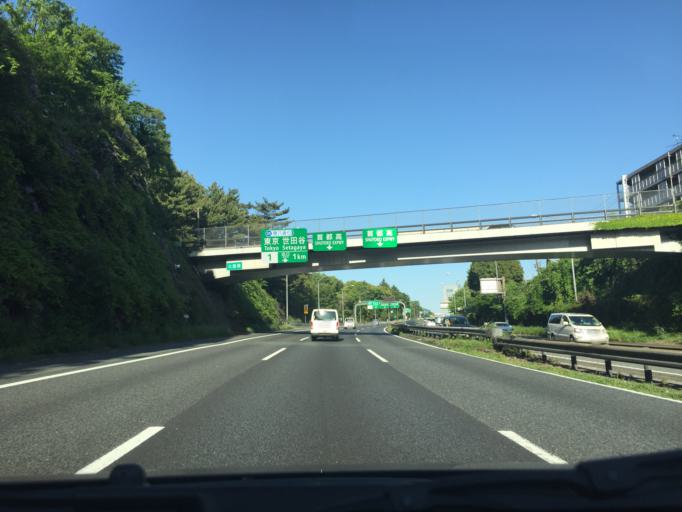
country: JP
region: Tokyo
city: Chofugaoka
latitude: 35.6286
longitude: 139.6139
